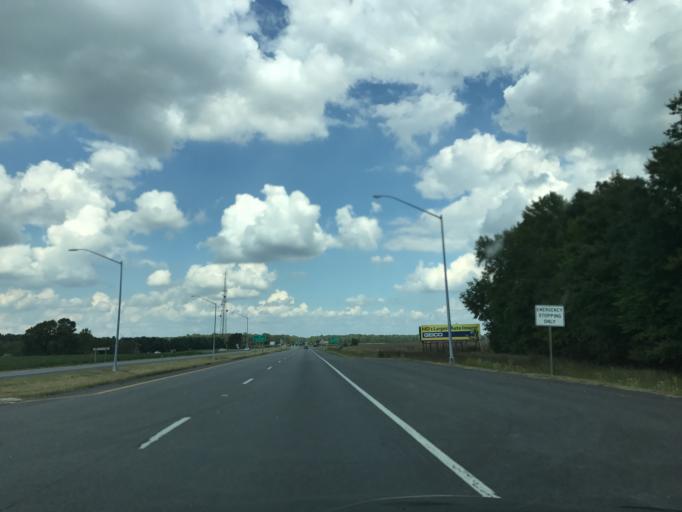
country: US
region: Maryland
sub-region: Queen Anne's County
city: Kingstown
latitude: 39.1688
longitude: -75.9184
